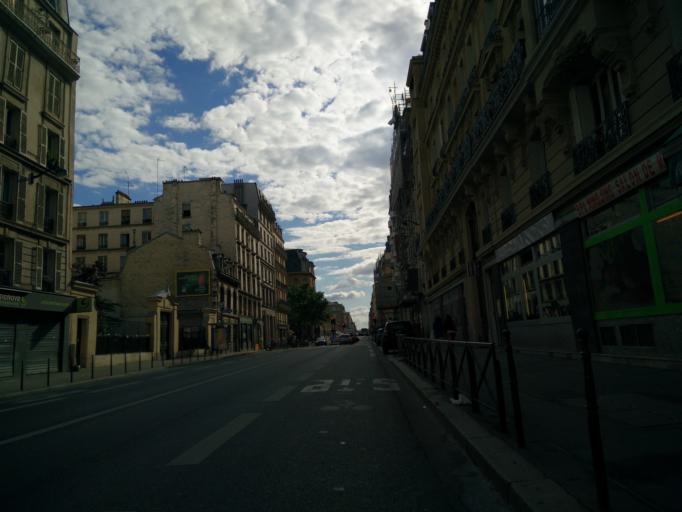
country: FR
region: Ile-de-France
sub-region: Paris
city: Paris
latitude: 48.8812
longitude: 2.3640
